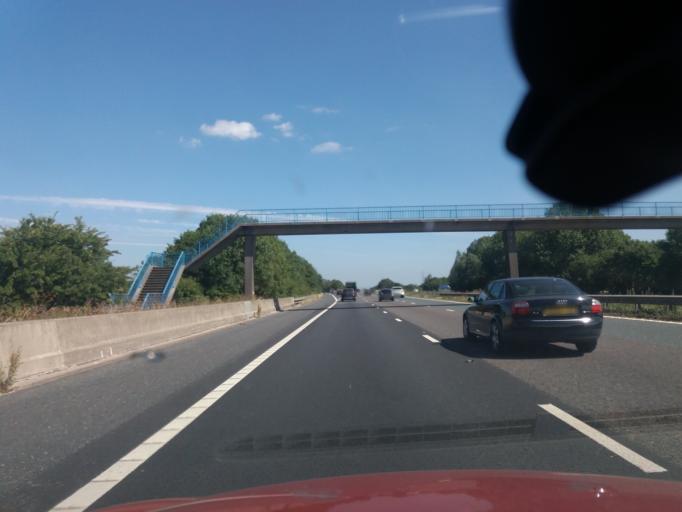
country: GB
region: England
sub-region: Borough of Wigan
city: Tyldesley
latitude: 53.5466
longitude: -2.4573
